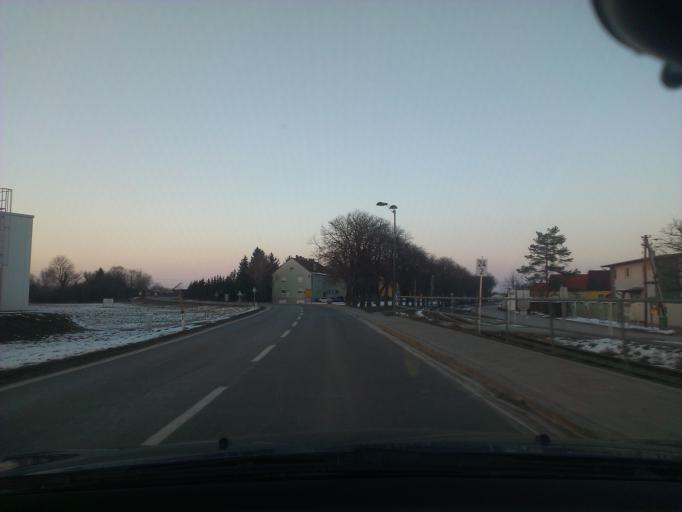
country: AT
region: Lower Austria
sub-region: Politischer Bezirk Bruck an der Leitha
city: Gotzendorf an der Leitha
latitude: 48.0160
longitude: 16.5825
